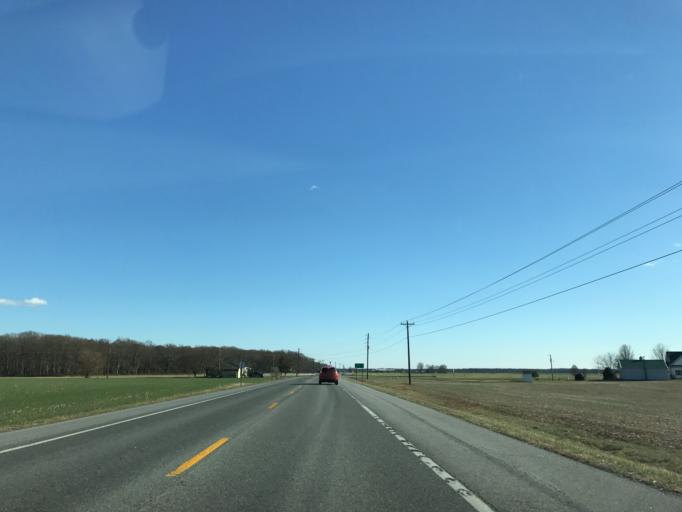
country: US
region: Maryland
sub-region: Caroline County
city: Greensboro
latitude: 39.0948
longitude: -75.8703
